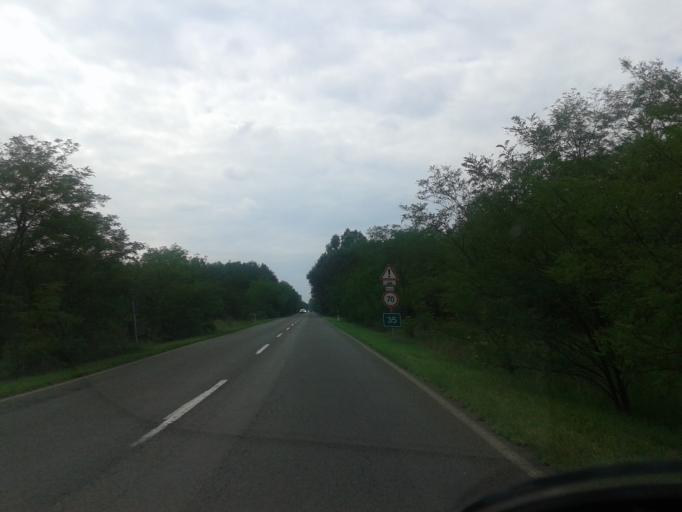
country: HU
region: Csongrad
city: Ruzsa
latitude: 46.2364
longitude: 19.7225
